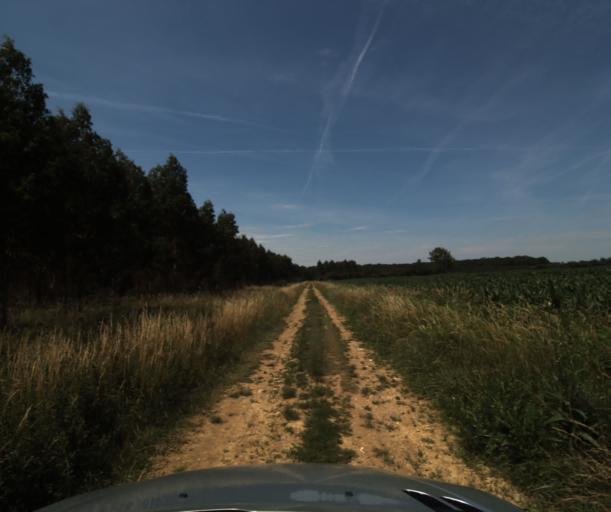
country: FR
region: Midi-Pyrenees
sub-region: Departement de la Haute-Garonne
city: Labastidette
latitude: 43.4560
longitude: 1.2320
